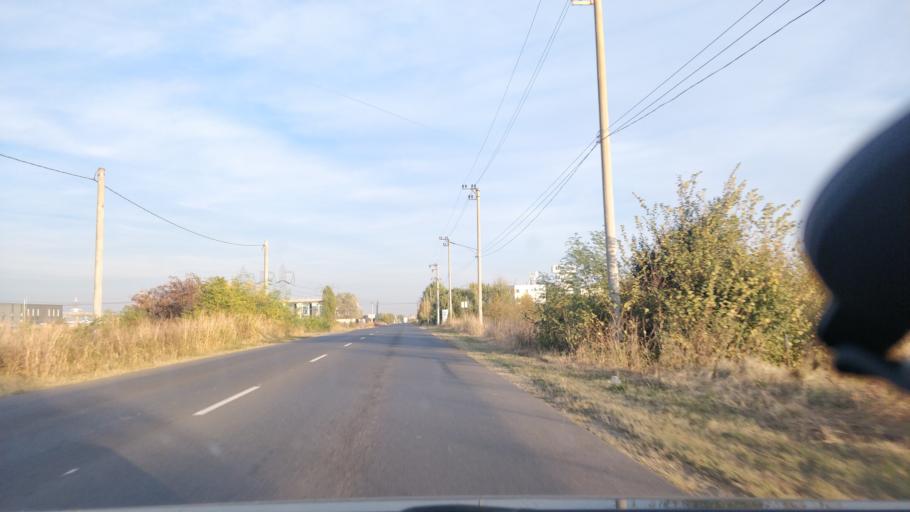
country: RO
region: Ilfov
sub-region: Comuna Ciorogarla
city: Ciorogarla
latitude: 44.4409
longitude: 25.9115
